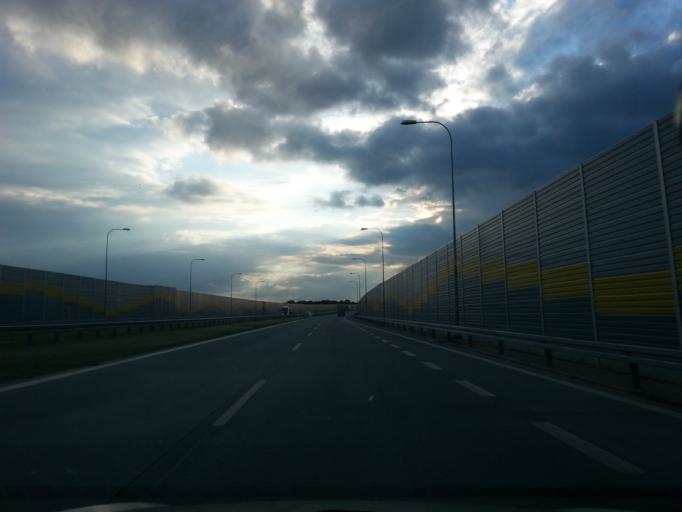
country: PL
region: Lodz Voivodeship
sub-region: Powiat zdunskowolski
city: Zdunska Wola
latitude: 51.5762
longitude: 18.9294
